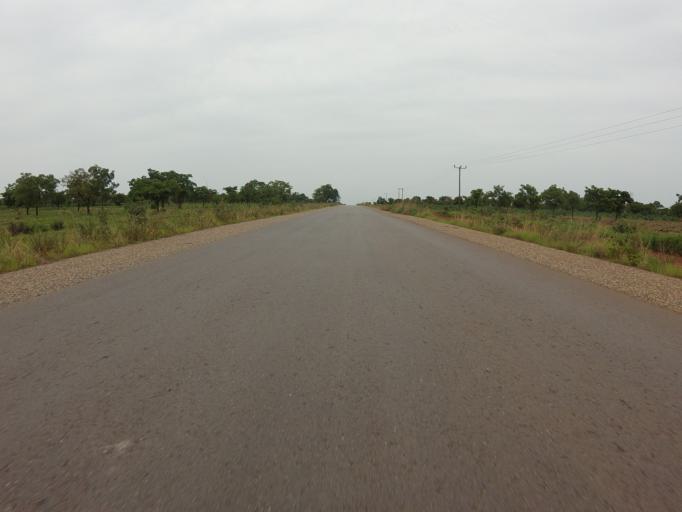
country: GH
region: Northern
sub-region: Yendi
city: Yendi
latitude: 9.2459
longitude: 0.0193
